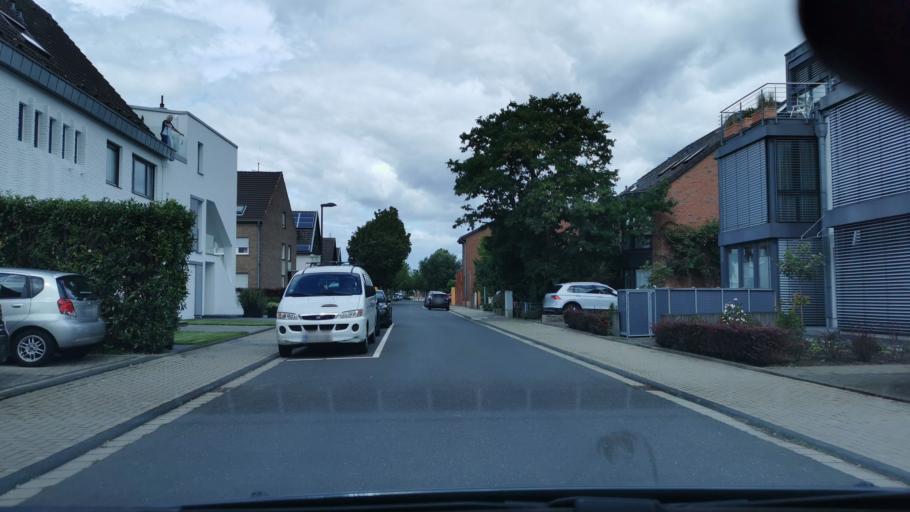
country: DE
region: North Rhine-Westphalia
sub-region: Regierungsbezirk Koln
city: Hurth
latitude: 50.8990
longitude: 6.8931
